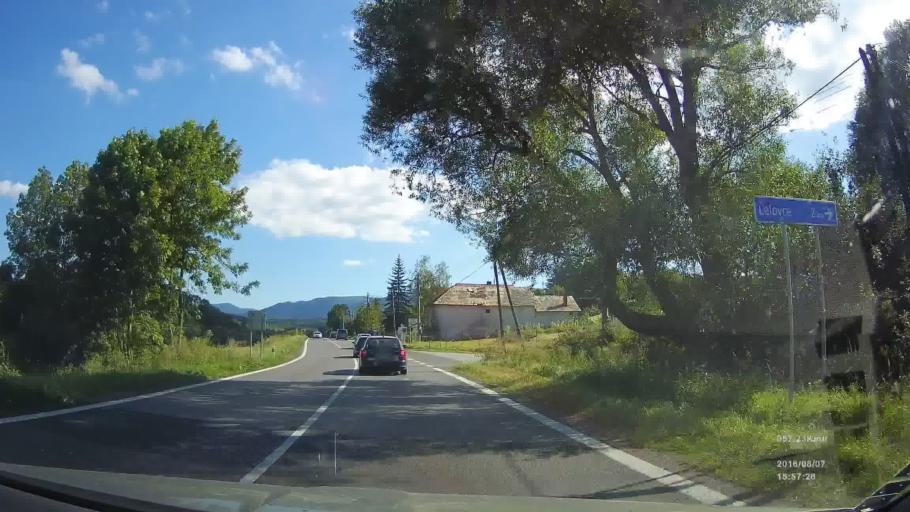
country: SK
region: Presovsky
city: Giraltovce
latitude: 49.0592
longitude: 21.4169
